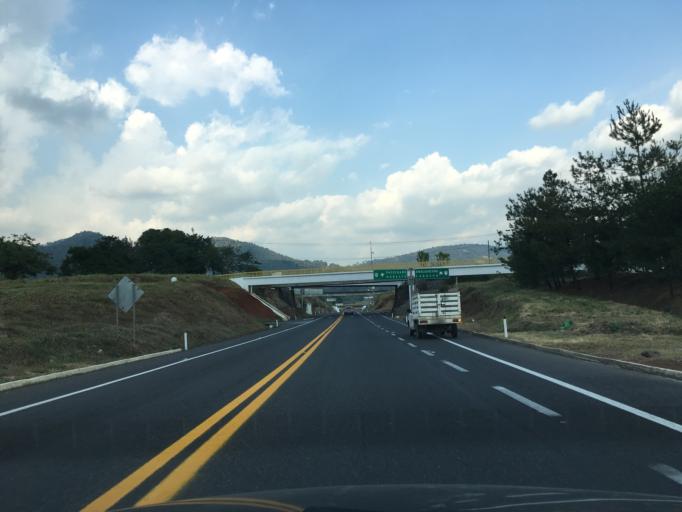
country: MX
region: Michoacan
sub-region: Ziracuaretiro
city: Patuan
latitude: 19.4229
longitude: -101.9241
